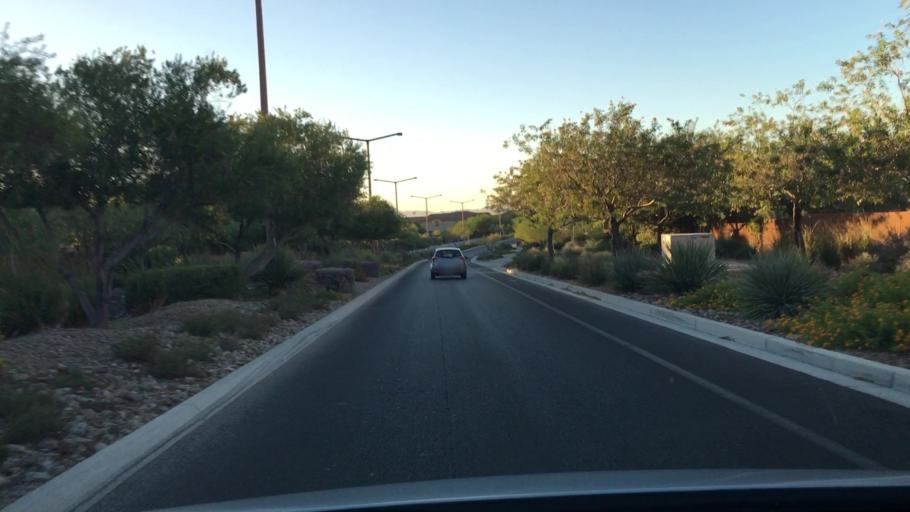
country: US
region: Nevada
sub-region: Clark County
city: Summerlin South
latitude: 36.0871
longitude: -115.3225
